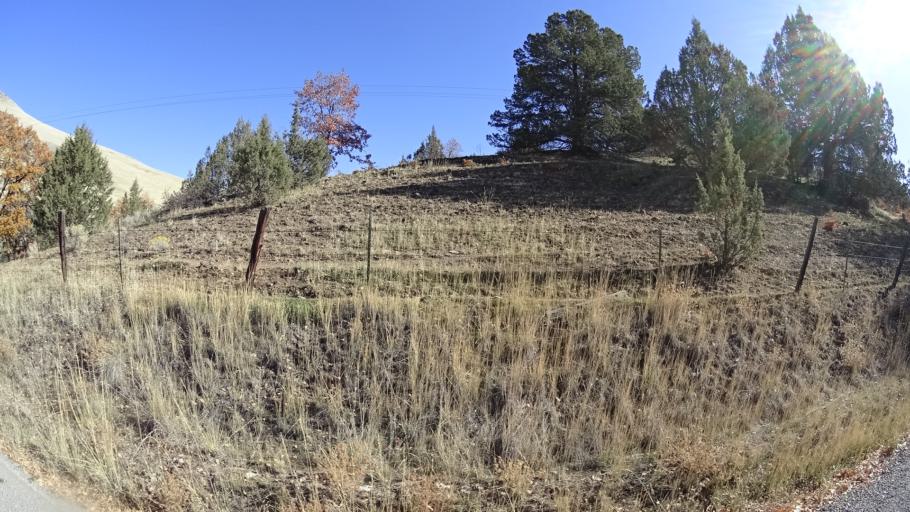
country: US
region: California
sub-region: Siskiyou County
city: Montague
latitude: 41.7924
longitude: -122.3610
